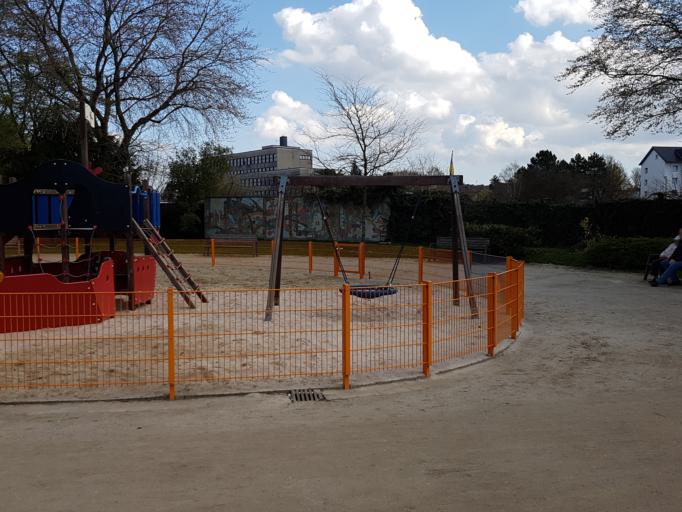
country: DE
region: North Rhine-Westphalia
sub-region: Regierungsbezirk Koln
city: Aachen
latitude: 50.7745
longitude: 6.1203
